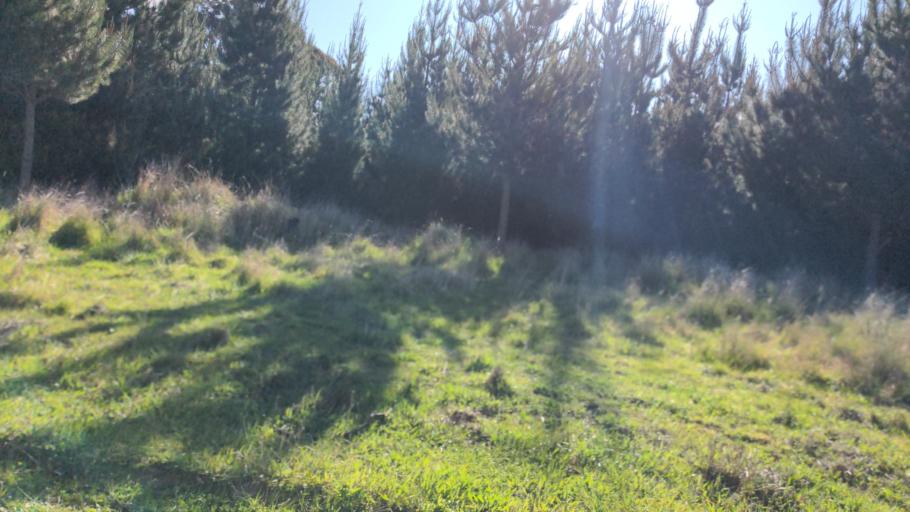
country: AU
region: New South Wales
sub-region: Blayney
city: Millthorpe
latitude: -33.4120
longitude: 149.3130
